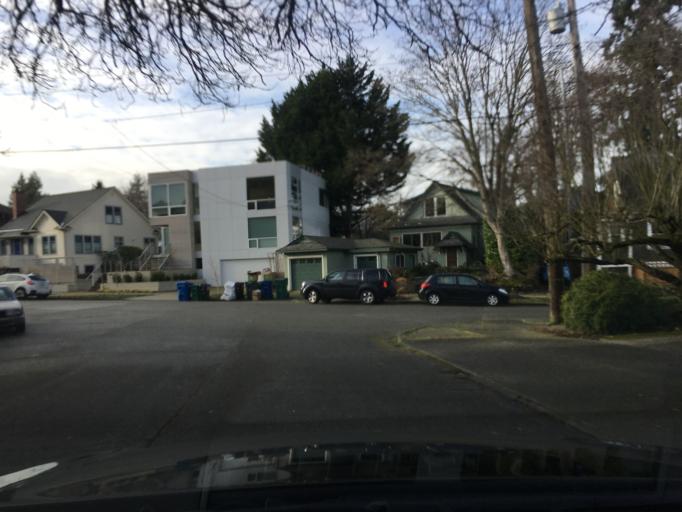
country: US
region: Washington
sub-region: King County
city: Seattle
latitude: 47.6709
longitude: -122.3367
